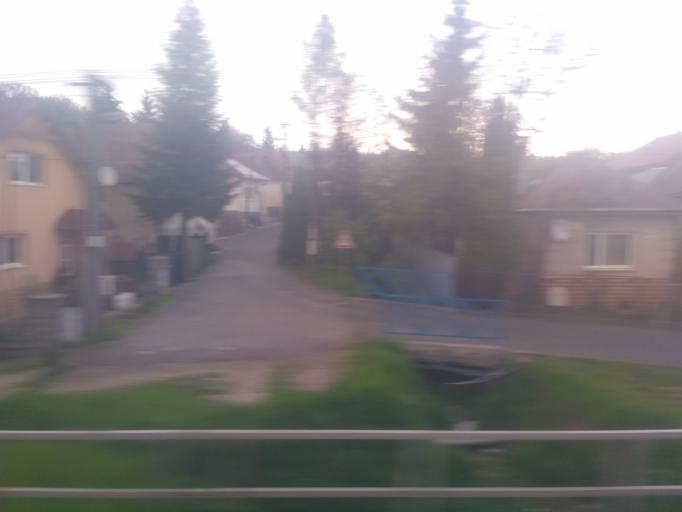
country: SK
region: Kosicky
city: Kosice
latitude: 48.7584
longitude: 21.2511
